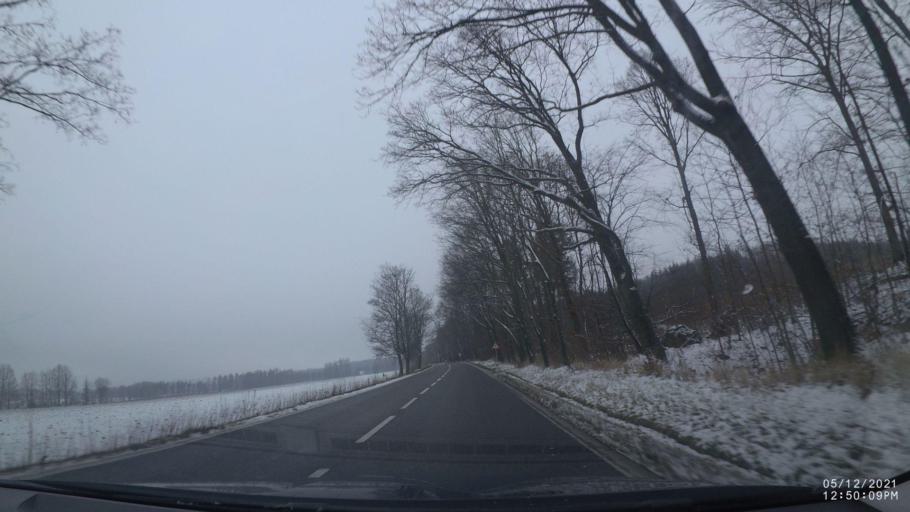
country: CZ
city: Nove Mesto nad Metuji
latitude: 50.3824
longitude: 16.1438
